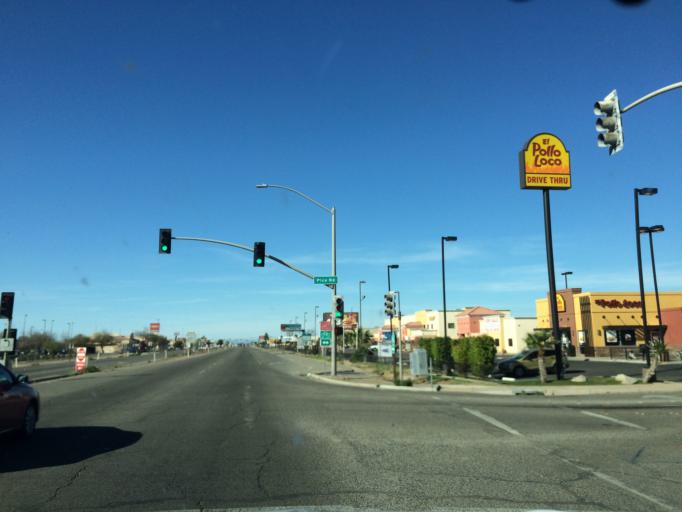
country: US
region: California
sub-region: Imperial County
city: El Centro
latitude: 32.8055
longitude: -115.5698
